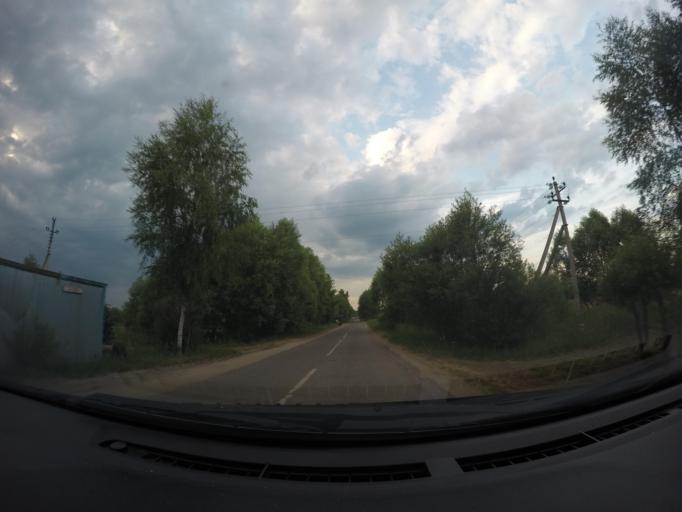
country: RU
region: Moskovskaya
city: Krasnyy Tkach
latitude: 55.4250
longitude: 39.2433
